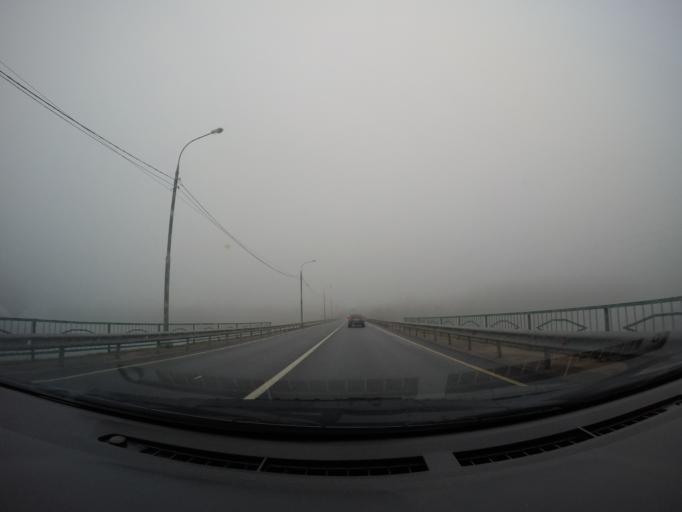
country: RU
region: Moskovskaya
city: Ruza
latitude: 55.7632
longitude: 36.2618
